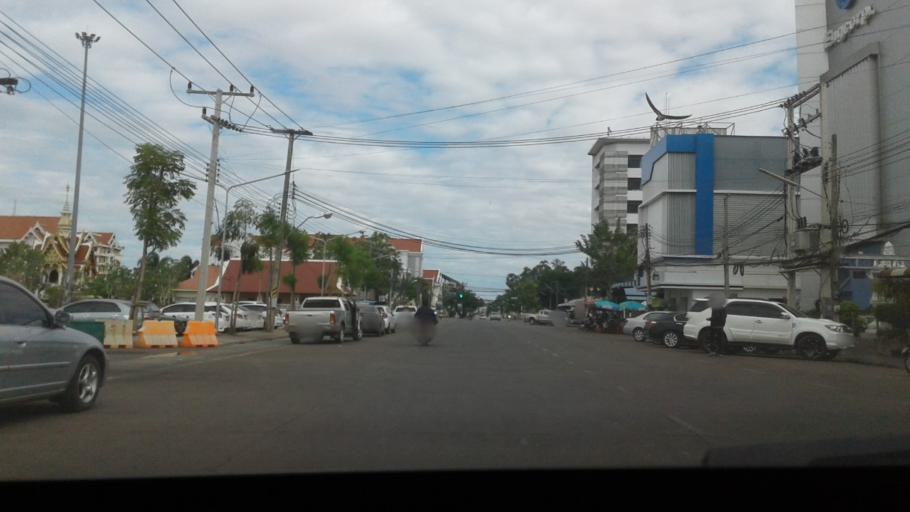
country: TH
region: Changwat Udon Thani
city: Udon Thani
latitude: 17.4120
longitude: 102.7876
